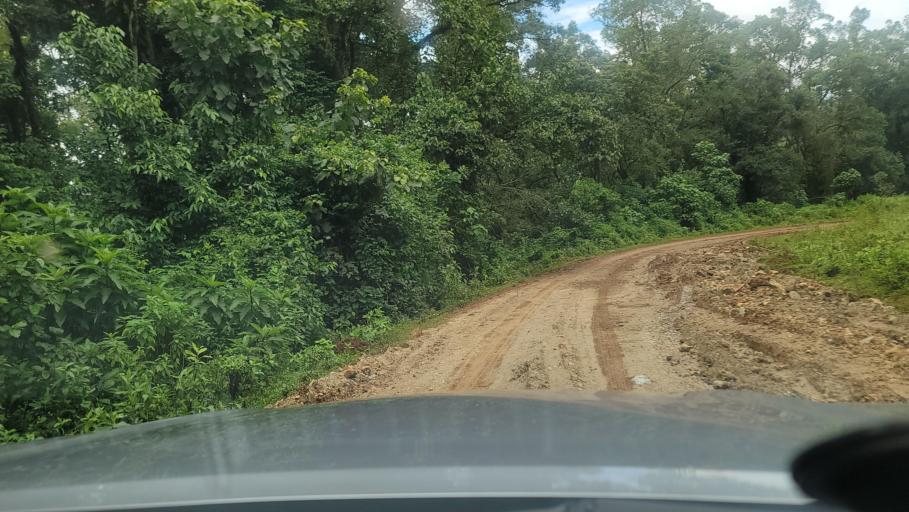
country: ET
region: Southern Nations, Nationalities, and People's Region
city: Bonga
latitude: 7.6229
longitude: 36.2106
